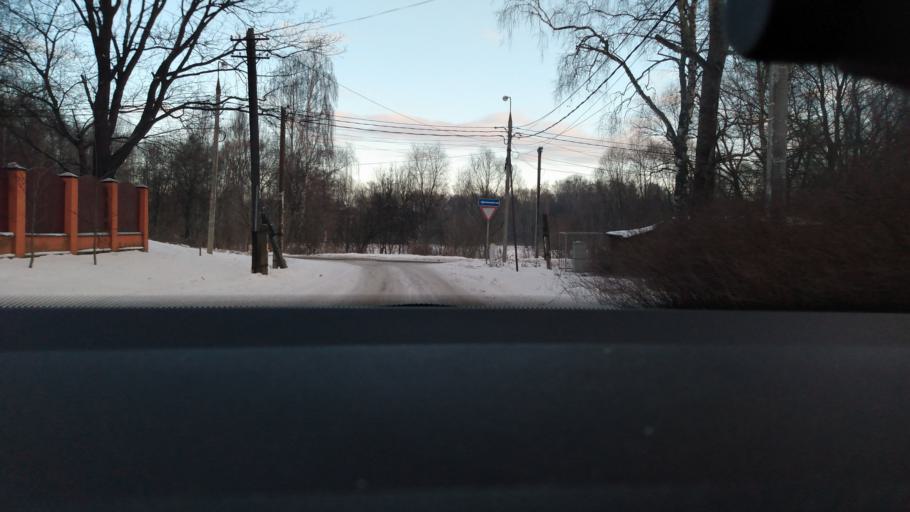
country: RU
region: Moskovskaya
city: Saltykovka
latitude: 55.7587
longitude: 37.9347
